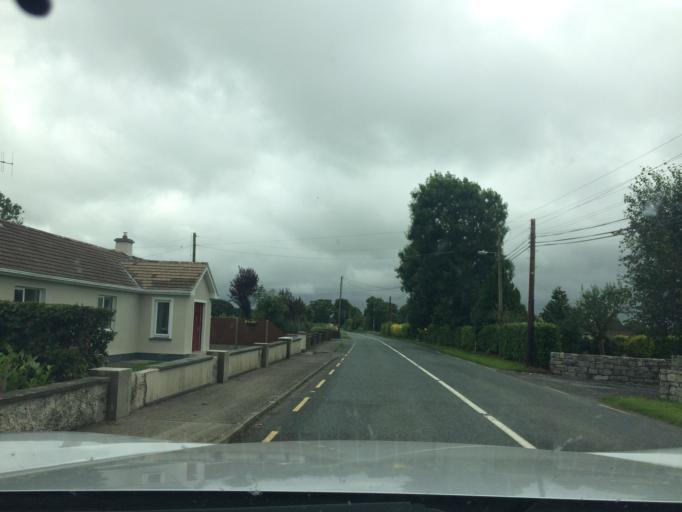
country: IE
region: Munster
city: Cashel
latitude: 52.5038
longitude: -7.8712
